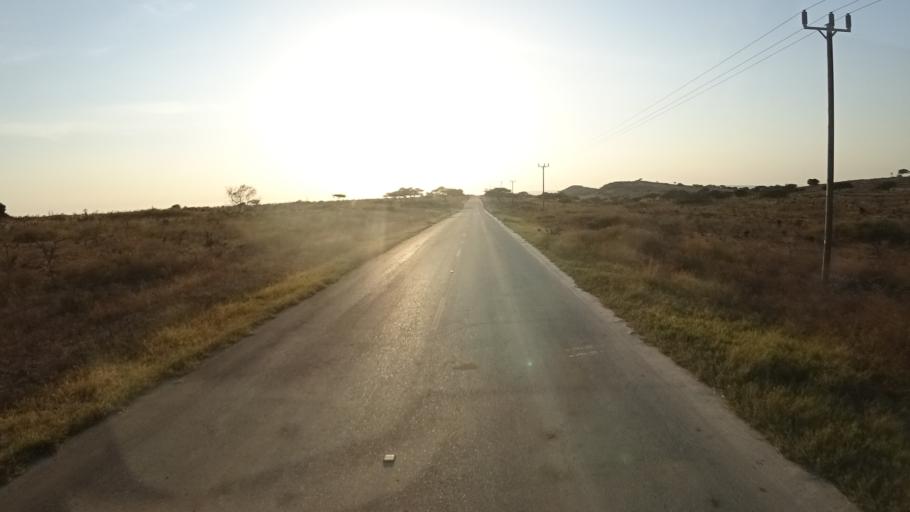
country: OM
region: Zufar
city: Salalah
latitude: 17.1476
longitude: 54.6135
